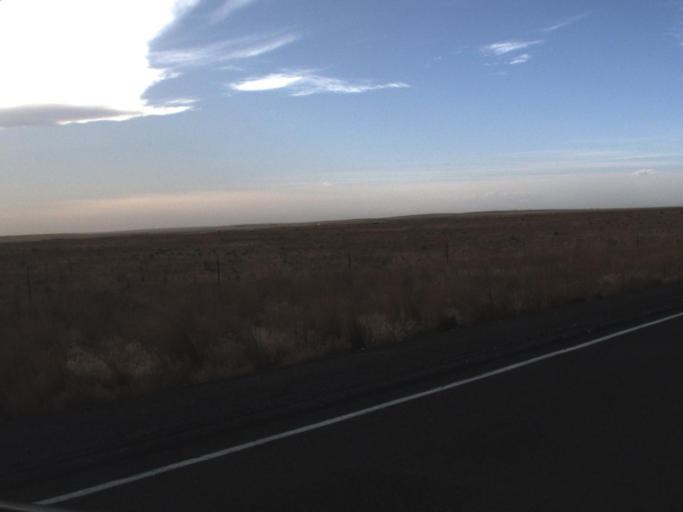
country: US
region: Washington
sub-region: Grant County
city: Warden
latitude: 47.3468
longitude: -118.9253
